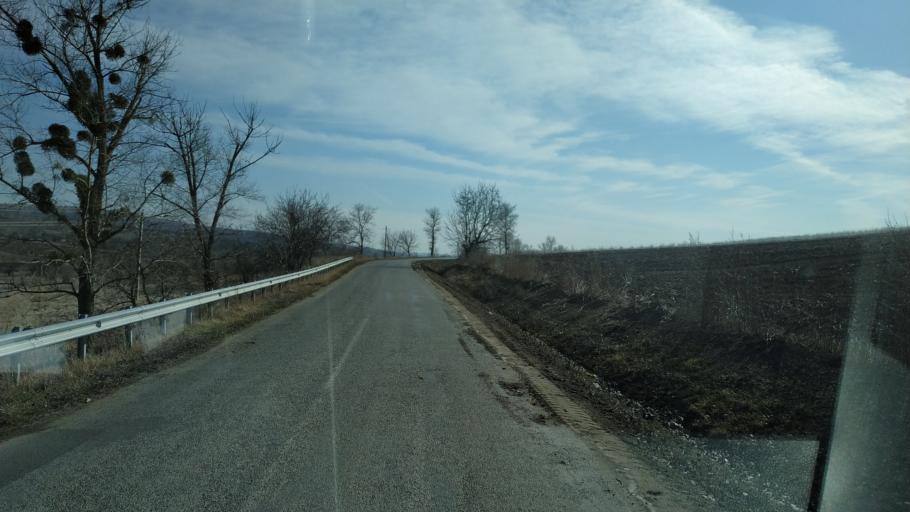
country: MD
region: Nisporeni
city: Nisporeni
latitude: 47.1219
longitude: 28.1201
